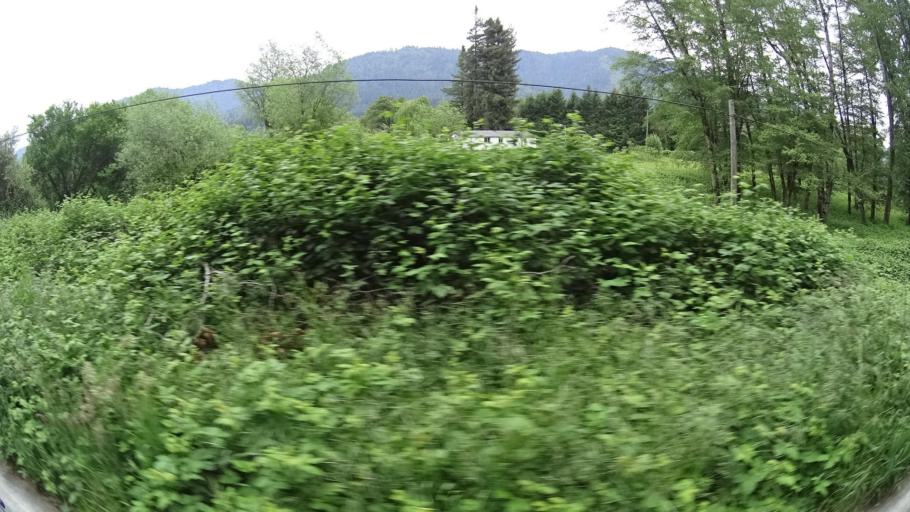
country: US
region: California
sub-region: Humboldt County
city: Willow Creek
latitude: 41.0601
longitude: -123.6925
